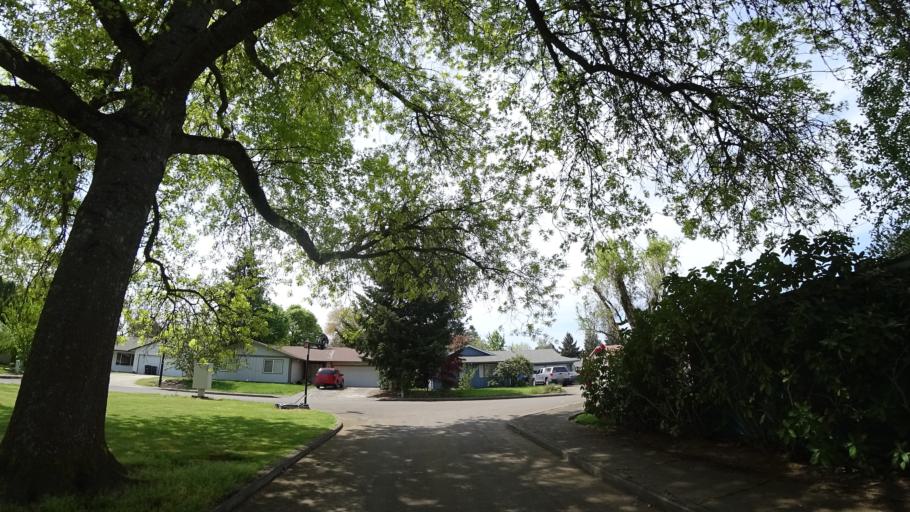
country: US
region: Oregon
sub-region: Washington County
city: Aloha
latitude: 45.4713
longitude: -122.8826
